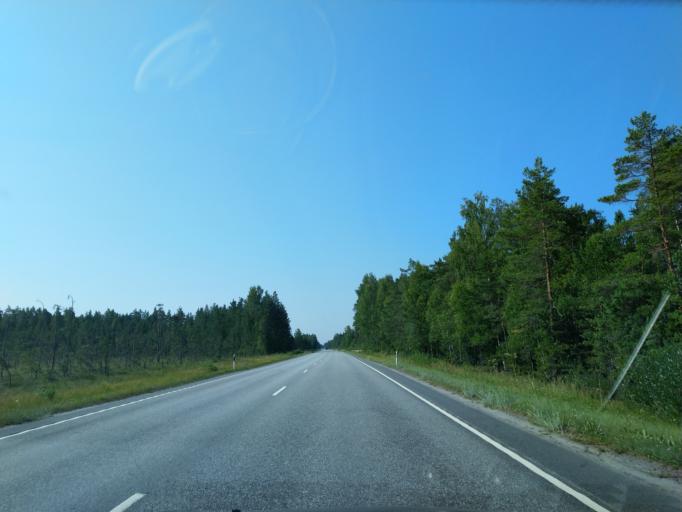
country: FI
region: Satakunta
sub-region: Pori
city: Pomarkku
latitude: 61.6818
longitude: 21.9895
